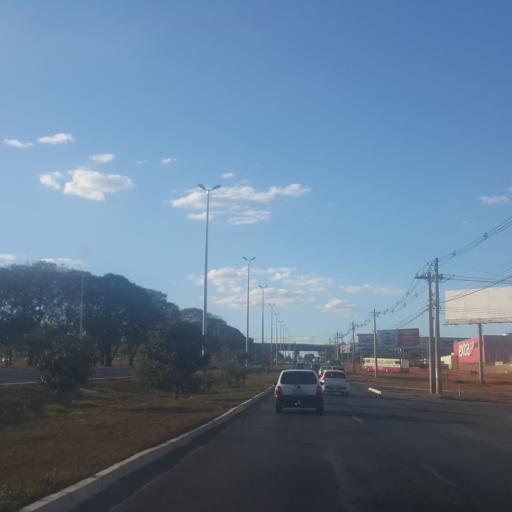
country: BR
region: Federal District
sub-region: Brasilia
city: Brasilia
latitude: -15.8364
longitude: -47.9522
